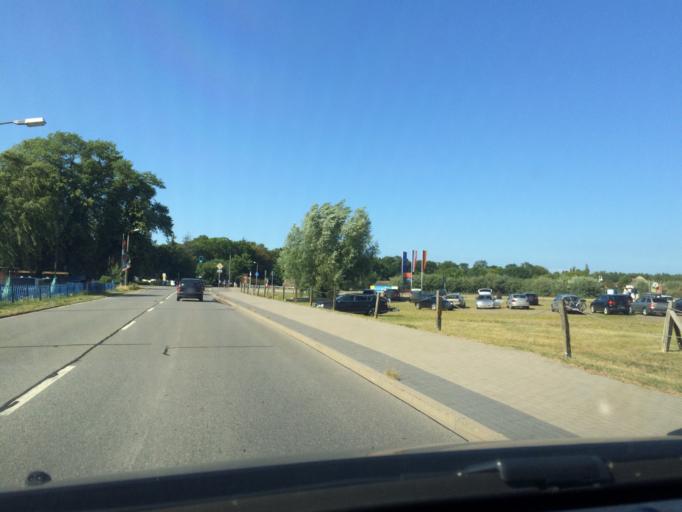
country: DE
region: Mecklenburg-Vorpommern
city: Ostseebad Prerow
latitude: 54.4438
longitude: 12.5831
